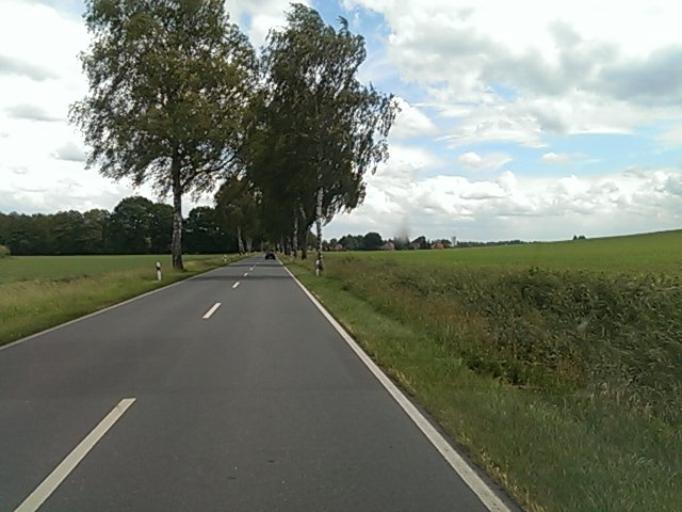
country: DE
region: Lower Saxony
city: Bergen
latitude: 52.7710
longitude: 10.0191
